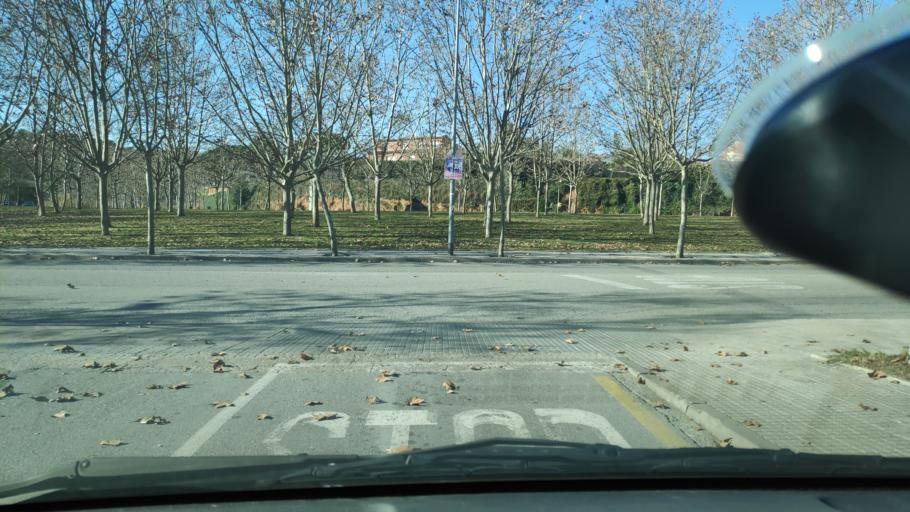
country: ES
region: Catalonia
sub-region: Provincia de Barcelona
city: Sant Quirze del Valles
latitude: 41.5291
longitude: 2.0874
